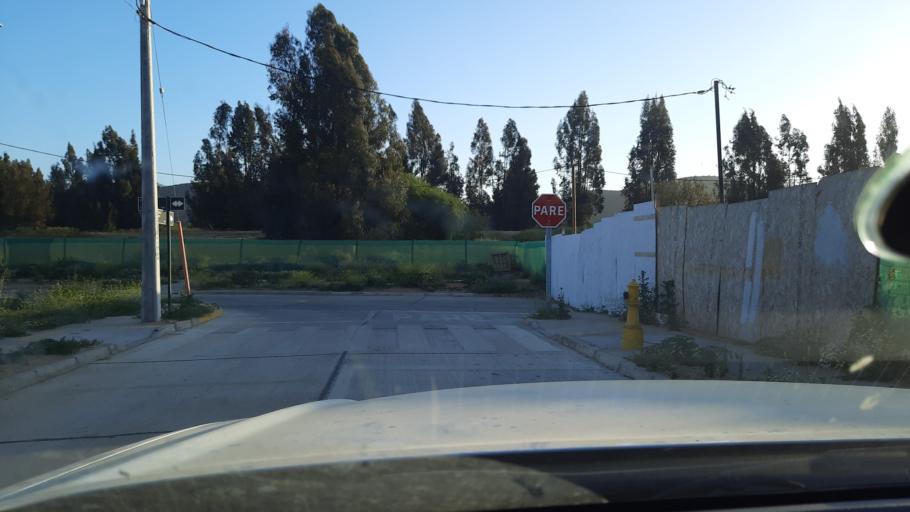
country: CL
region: Valparaiso
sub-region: Provincia de Marga Marga
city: Limache
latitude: -32.9958
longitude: -71.2796
